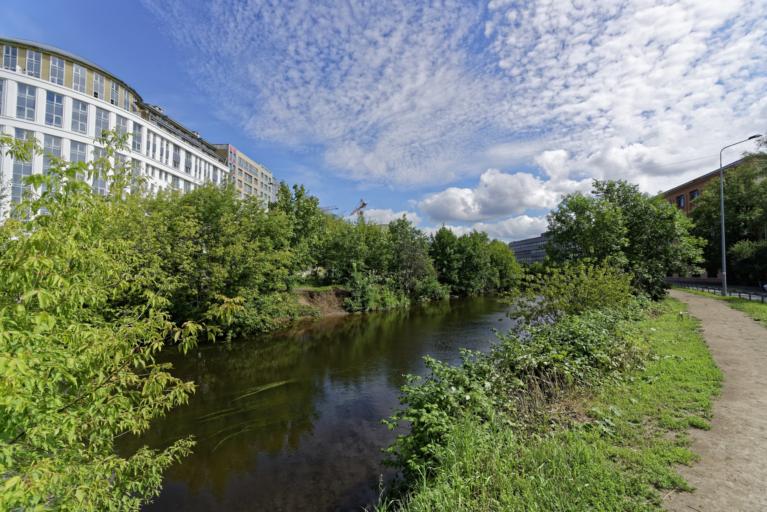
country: RU
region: St.-Petersburg
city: Vasyl'evsky Ostrov
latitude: 59.9478
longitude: 30.2636
